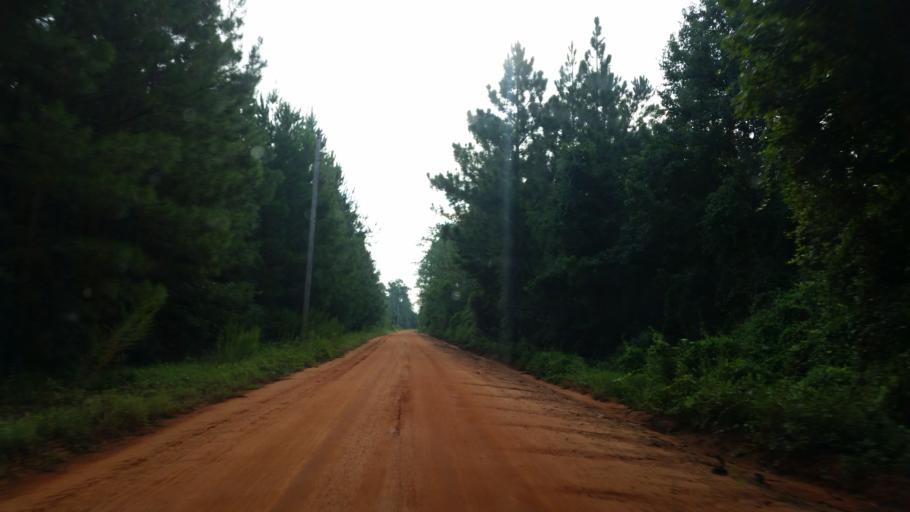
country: US
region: Florida
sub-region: Escambia County
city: Molino
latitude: 30.7920
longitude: -87.5307
